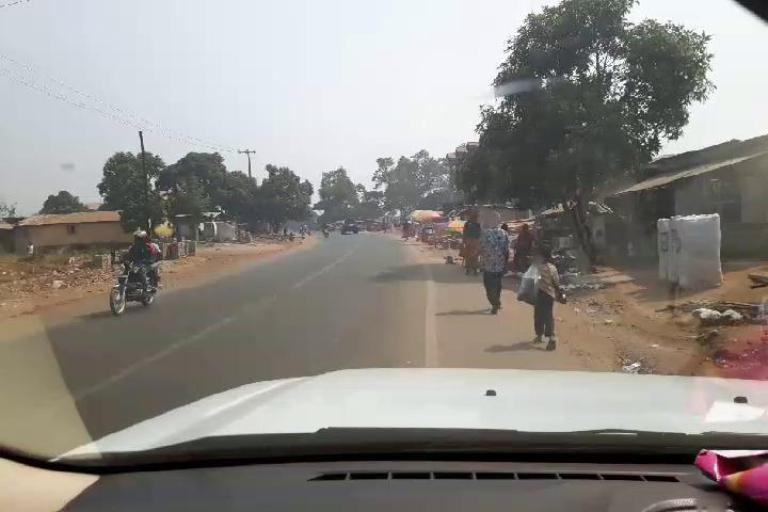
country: SL
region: Western Area
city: Waterloo
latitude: 8.3209
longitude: -13.0728
